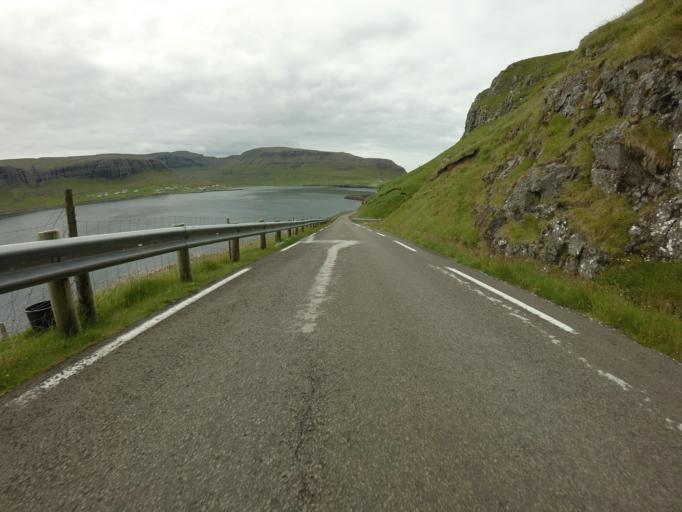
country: FO
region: Suduroy
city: Tvoroyri
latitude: 61.6083
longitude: -6.9288
